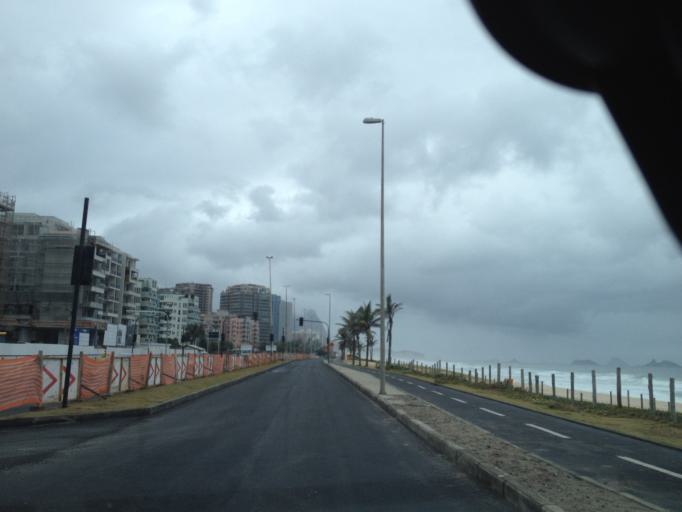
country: BR
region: Rio de Janeiro
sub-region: Rio De Janeiro
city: Rio de Janeiro
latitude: -23.0113
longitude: -43.3734
